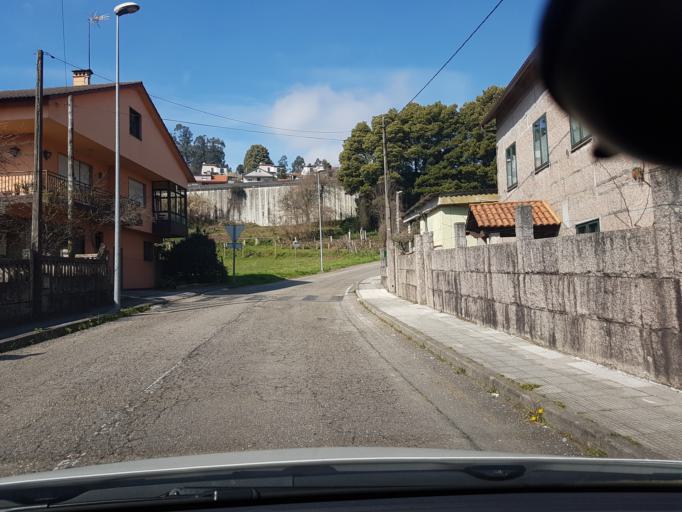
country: ES
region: Galicia
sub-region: Provincia de Pontevedra
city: Porrino
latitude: 42.1953
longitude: -8.6515
